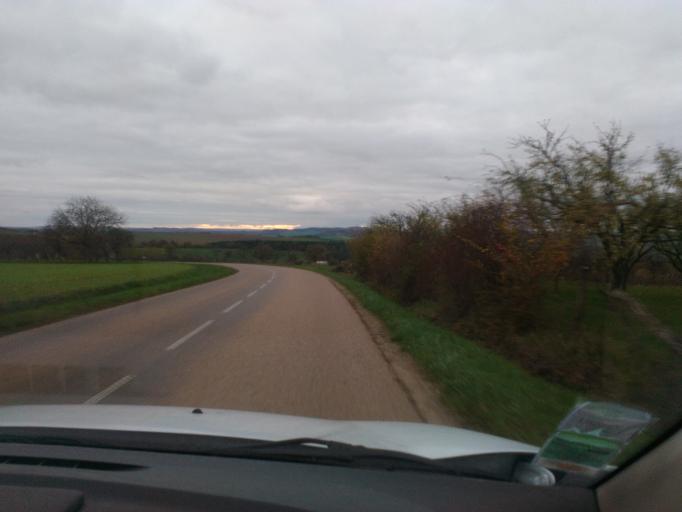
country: FR
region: Lorraine
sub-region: Departement des Vosges
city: Mirecourt
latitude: 48.2913
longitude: 6.1975
